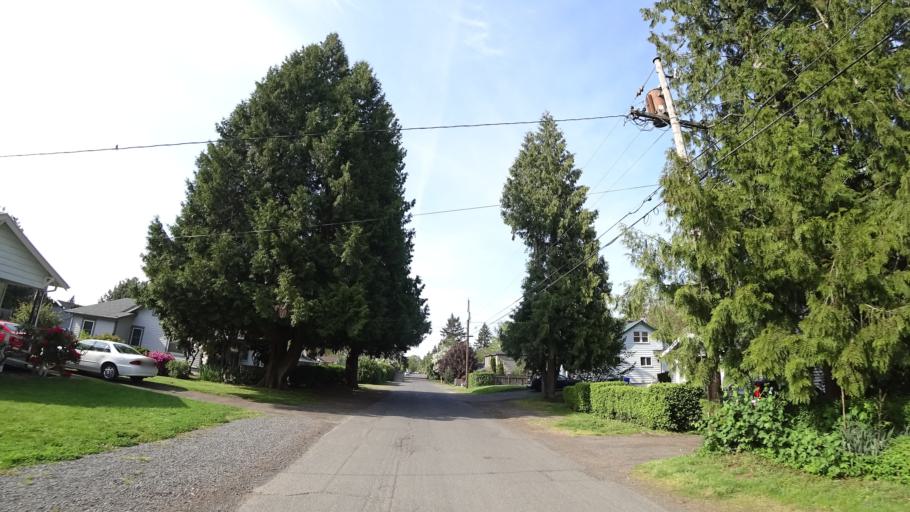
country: US
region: Oregon
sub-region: Clackamas County
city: Milwaukie
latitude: 45.4736
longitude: -122.6134
